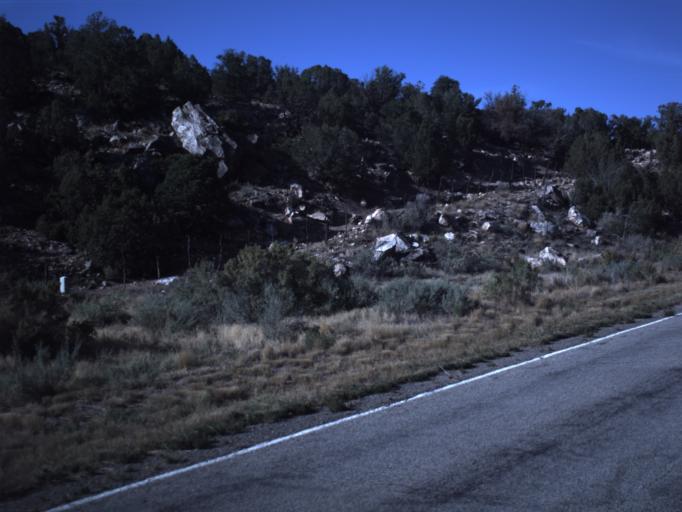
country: US
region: Utah
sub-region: Grand County
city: Moab
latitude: 38.3116
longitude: -109.3547
